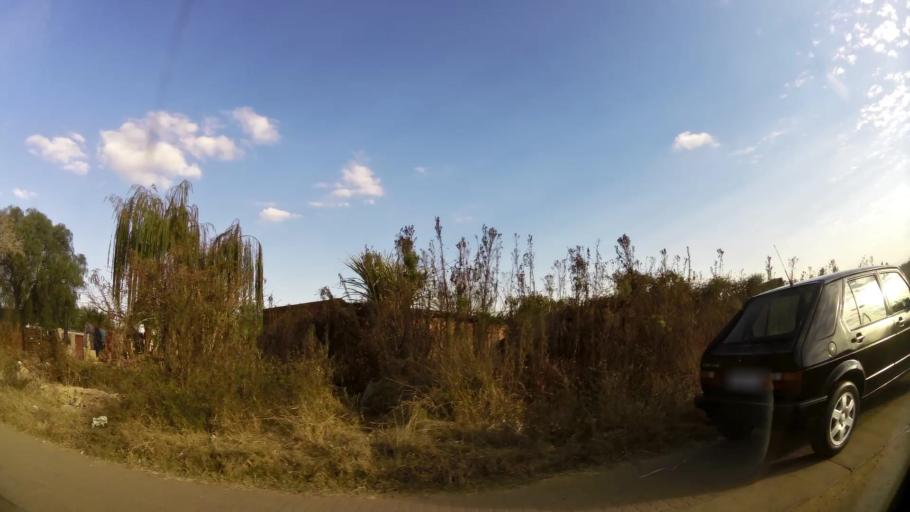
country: ZA
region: Gauteng
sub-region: City of Tshwane Metropolitan Municipality
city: Cullinan
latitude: -25.7093
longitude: 28.3762
